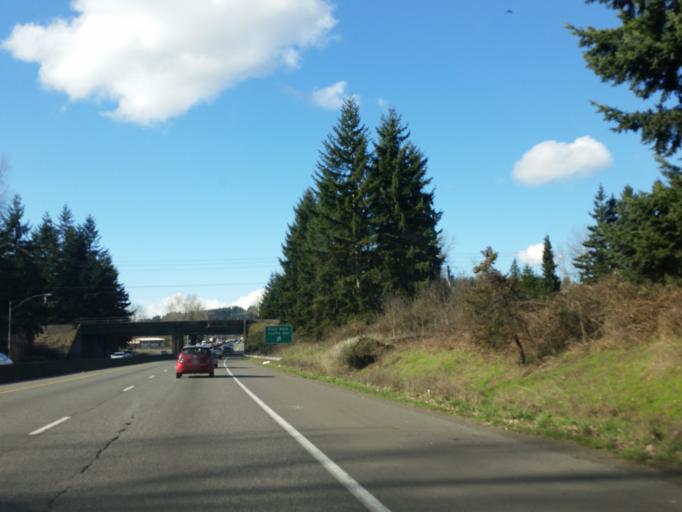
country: US
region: Washington
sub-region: Pierce County
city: Sumner
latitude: 47.1970
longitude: -122.2471
